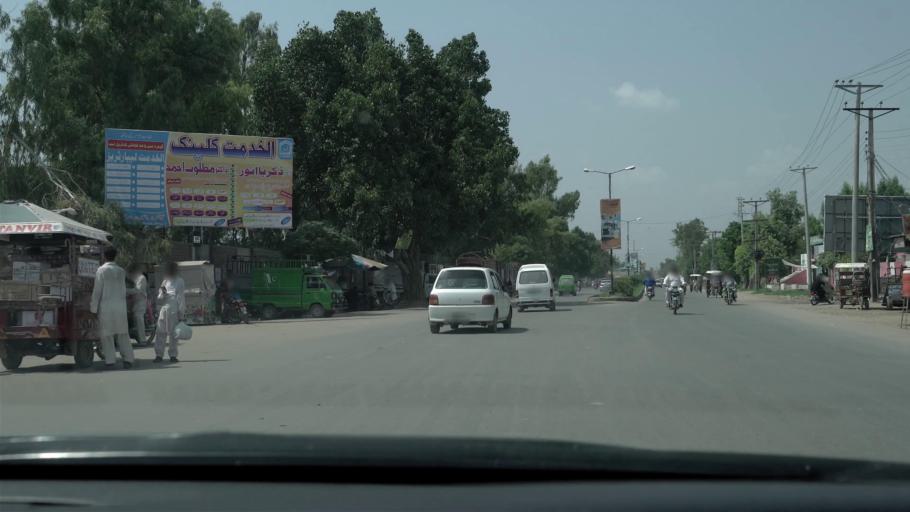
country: PK
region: Punjab
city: Gojra
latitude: 31.1529
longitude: 72.6736
